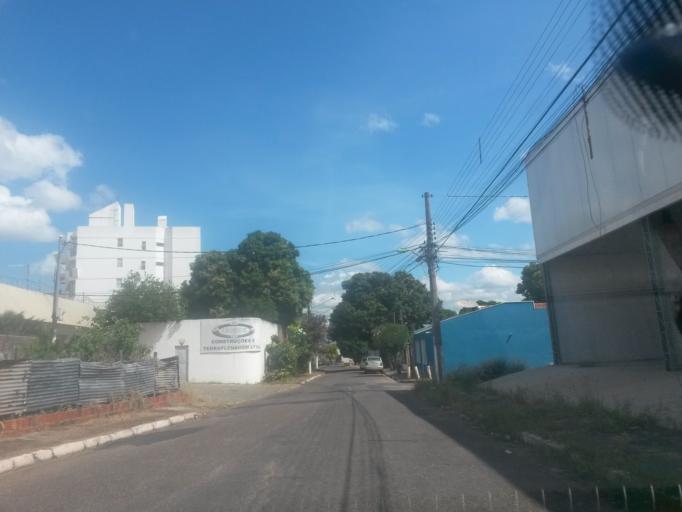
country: BR
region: Mato Grosso
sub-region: Cuiaba
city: Cuiaba
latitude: -15.6110
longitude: -56.0826
